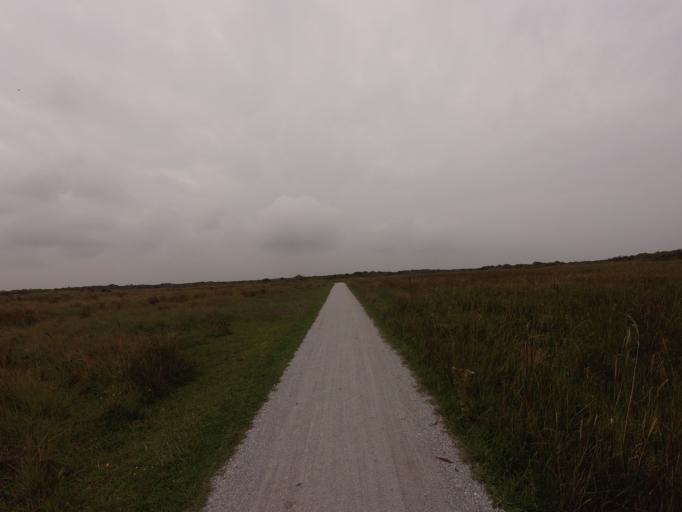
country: NL
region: Friesland
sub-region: Gemeente Schiermonnikoog
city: Schiermonnikoog
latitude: 53.4888
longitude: 6.2067
